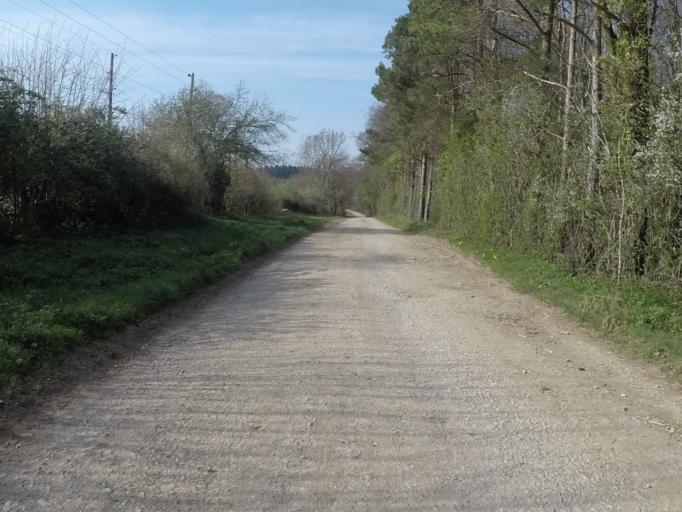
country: GB
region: England
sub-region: Oxfordshire
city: Charlbury
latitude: 51.8842
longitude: -1.4510
